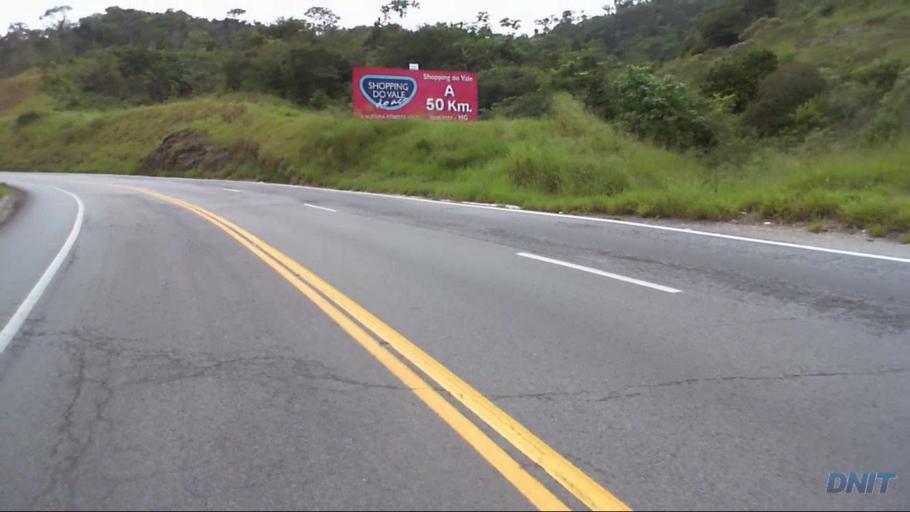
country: BR
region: Minas Gerais
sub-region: Nova Era
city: Nova Era
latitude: -19.6460
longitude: -42.9055
